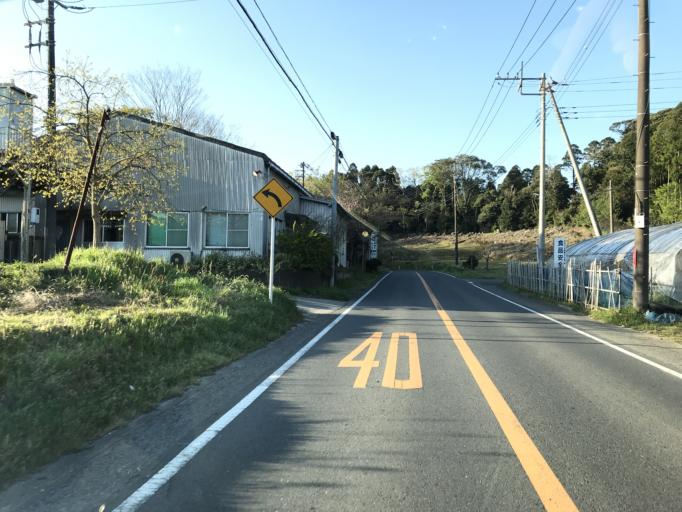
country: JP
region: Chiba
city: Yokaichiba
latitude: 35.7297
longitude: 140.5606
